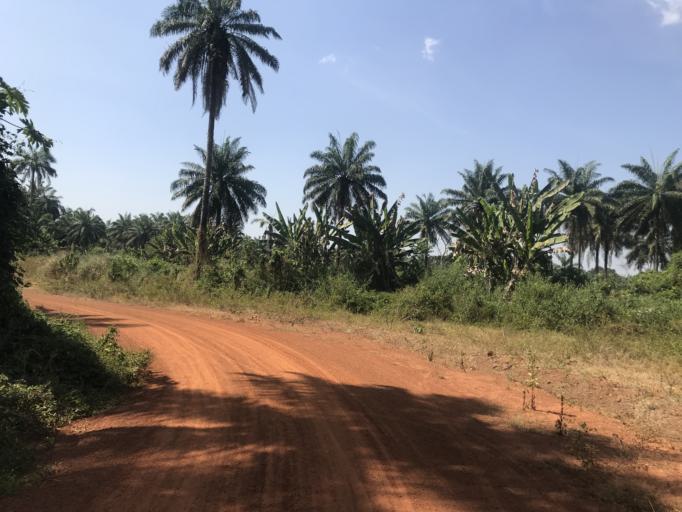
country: NG
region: Osun
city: Ikirun
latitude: 7.9341
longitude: 4.6236
